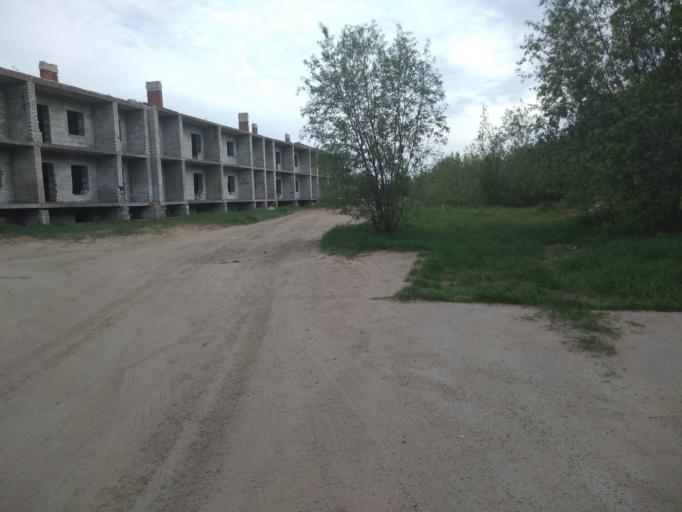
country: RU
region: Komi Republic
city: Pechora
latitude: 65.1412
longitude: 57.2452
